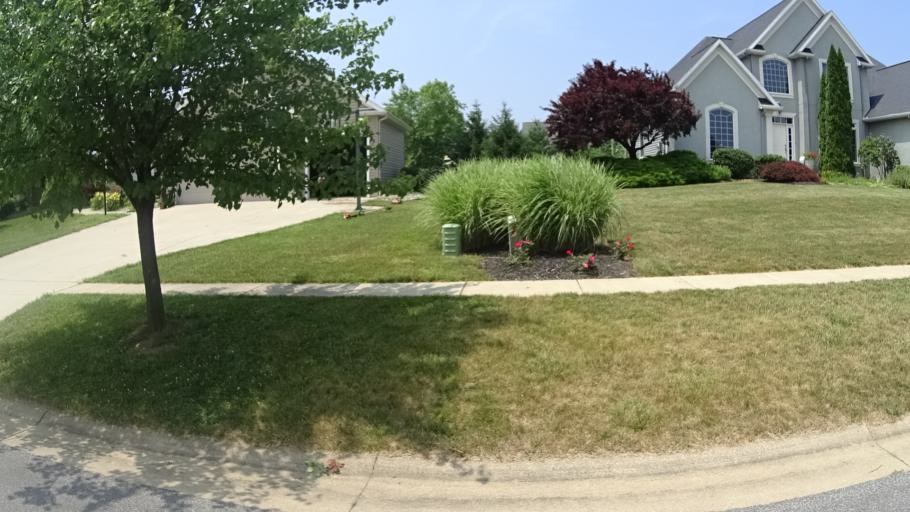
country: US
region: Ohio
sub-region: Erie County
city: Huron
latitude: 41.3831
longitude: -82.5308
